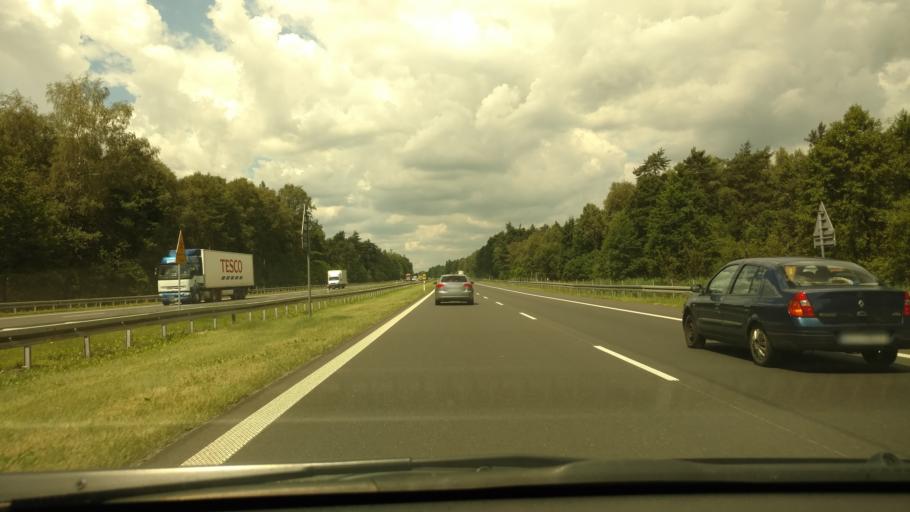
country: PL
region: Lesser Poland Voivodeship
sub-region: Powiat chrzanowski
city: Bolecin
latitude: 50.1282
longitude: 19.4833
